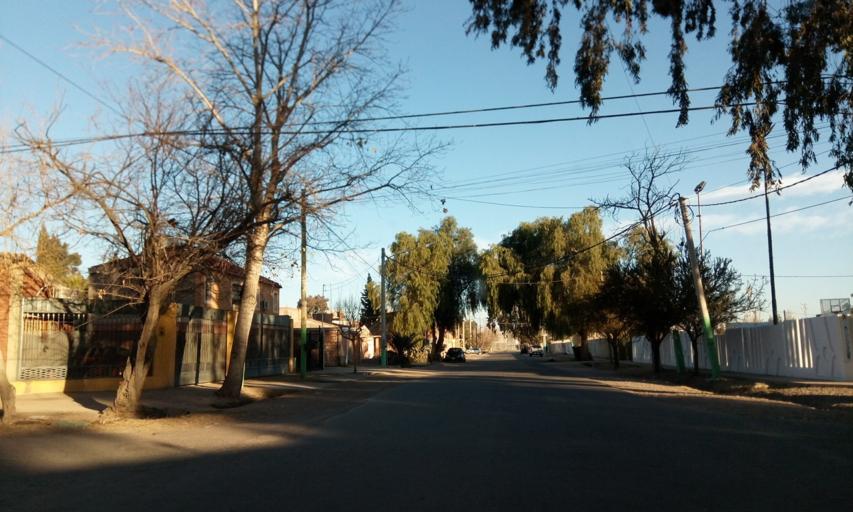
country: AR
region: San Juan
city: San Juan
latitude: -31.5363
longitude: -68.5905
